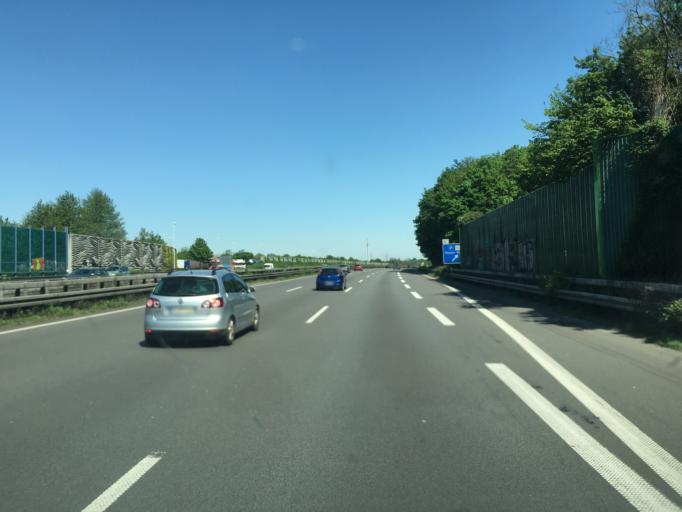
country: DE
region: North Rhine-Westphalia
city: Herten
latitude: 51.5698
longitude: 7.0948
